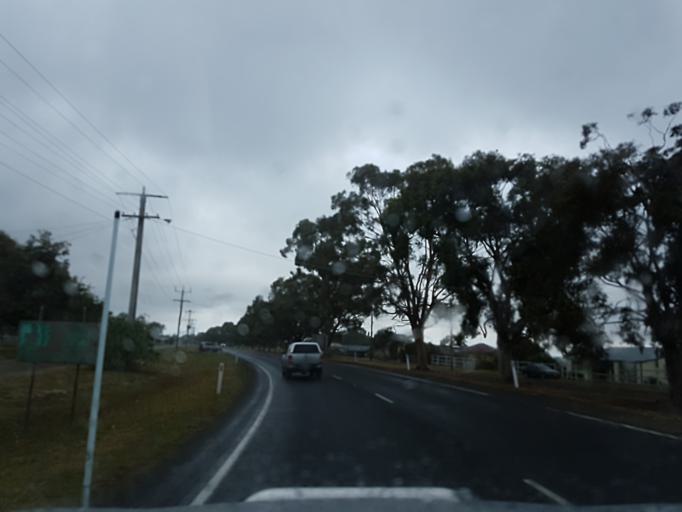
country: AU
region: Victoria
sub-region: East Gippsland
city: Bairnsdale
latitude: -37.8114
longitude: 147.6474
